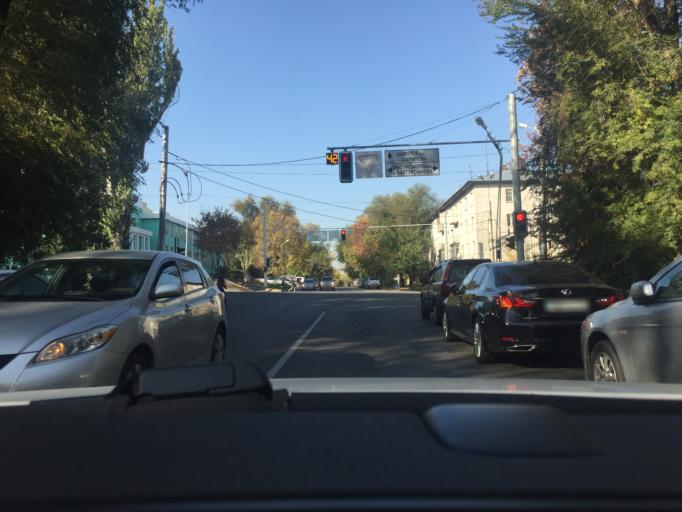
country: KZ
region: Almaty Qalasy
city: Almaty
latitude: 43.2467
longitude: 76.9273
